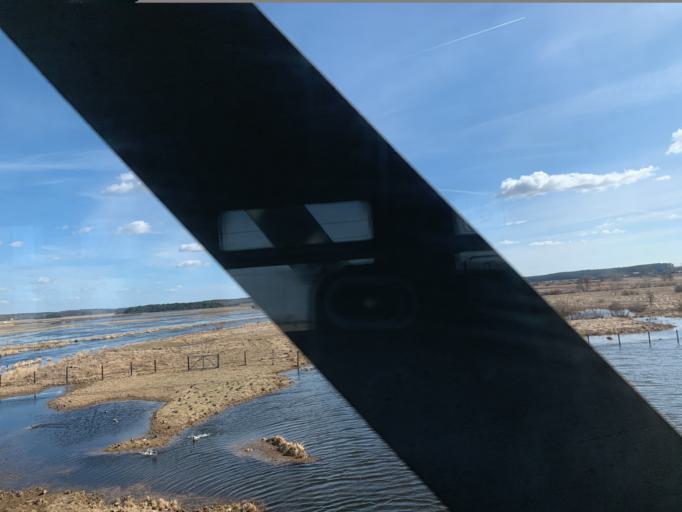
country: BY
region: Minsk
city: Novy Svyerzhan'
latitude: 53.4677
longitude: 26.7313
